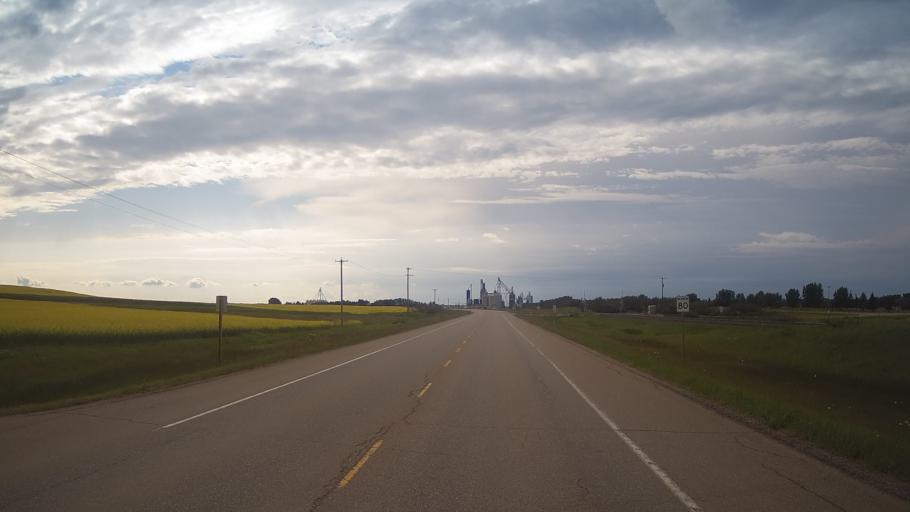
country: CA
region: Alberta
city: Viking
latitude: 53.0858
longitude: -111.7570
